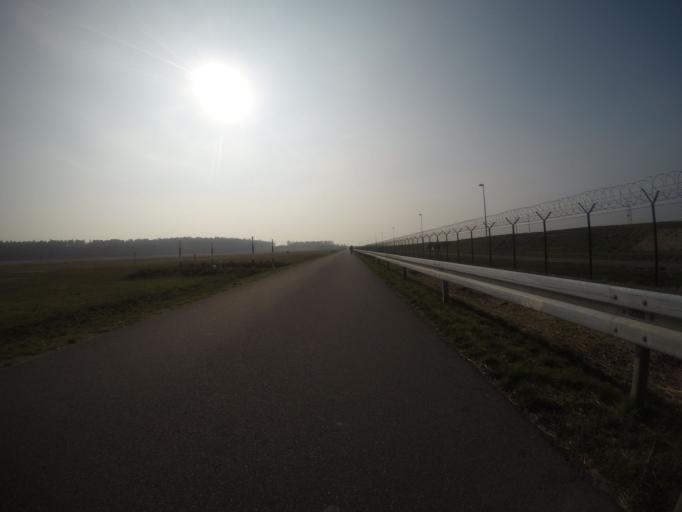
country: DE
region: Brandenburg
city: Schonefeld
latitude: 52.3442
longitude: 13.4759
